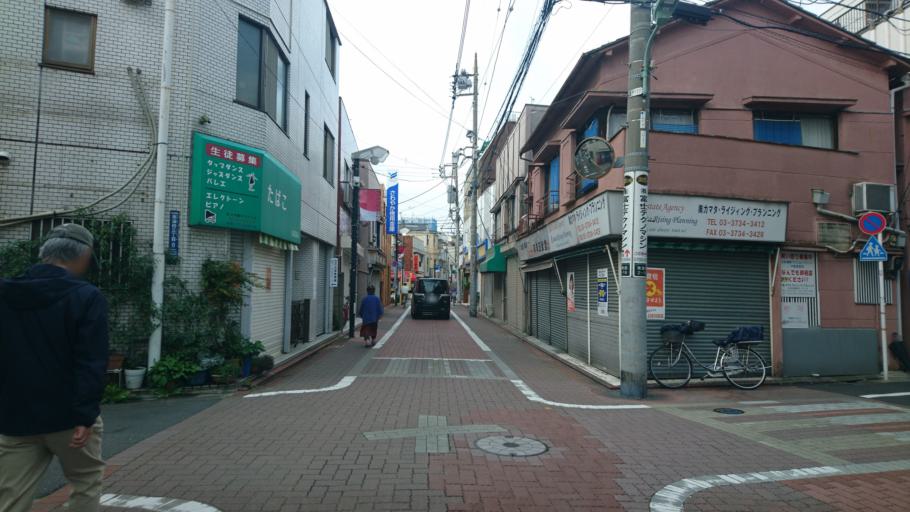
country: JP
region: Kanagawa
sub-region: Kawasaki-shi
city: Kawasaki
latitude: 35.5544
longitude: 139.7250
